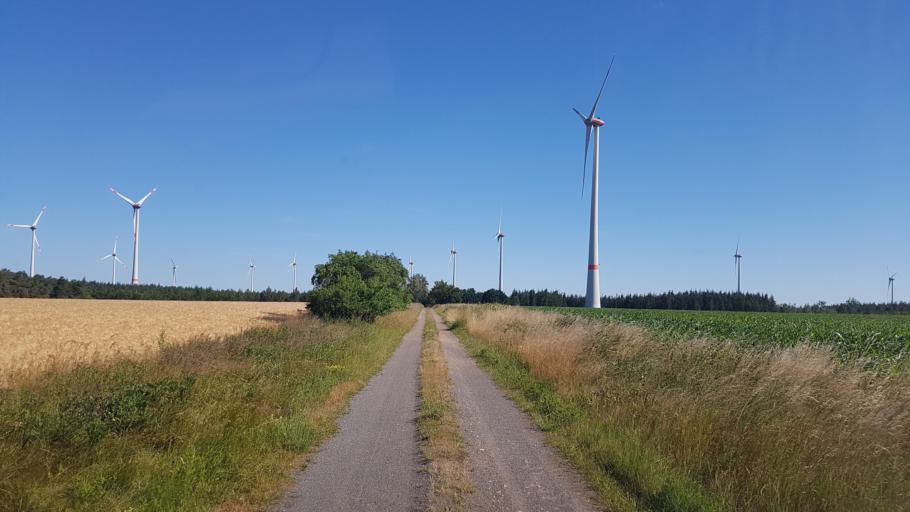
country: DE
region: Brandenburg
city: Treuenbrietzen
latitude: 52.0060
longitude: 12.8572
